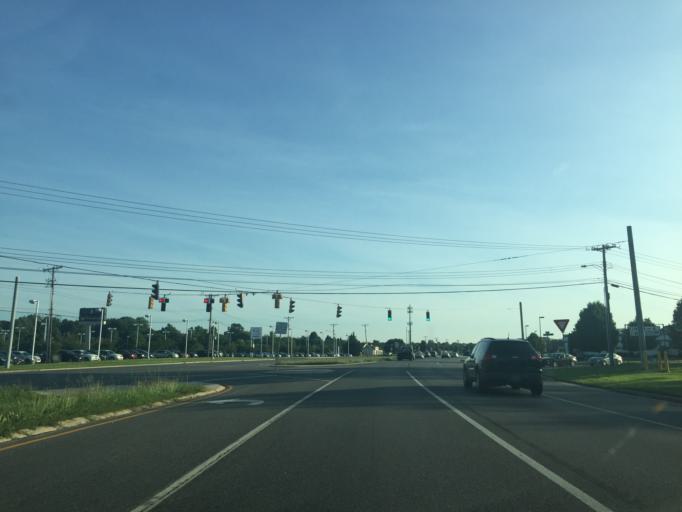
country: US
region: Delaware
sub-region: Kent County
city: Kent Acres
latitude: 39.1436
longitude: -75.5179
